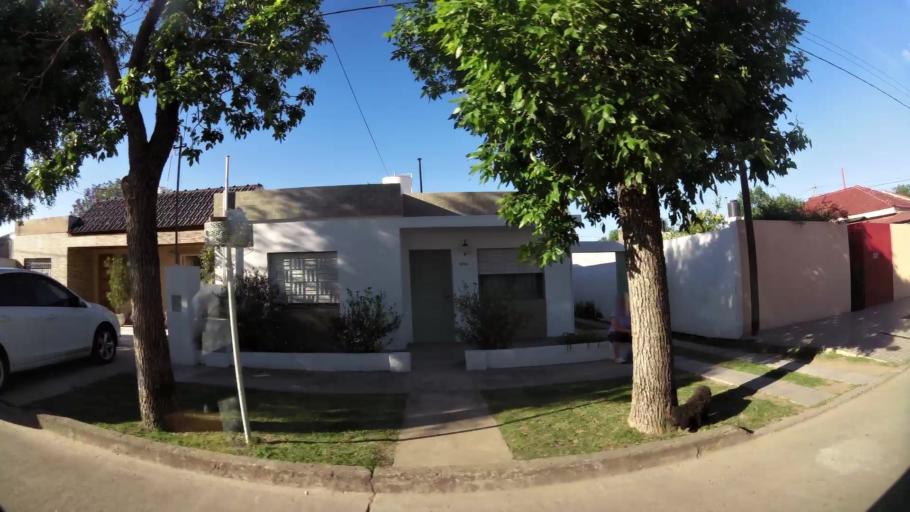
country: AR
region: Cordoba
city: San Francisco
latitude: -31.4440
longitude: -62.0956
